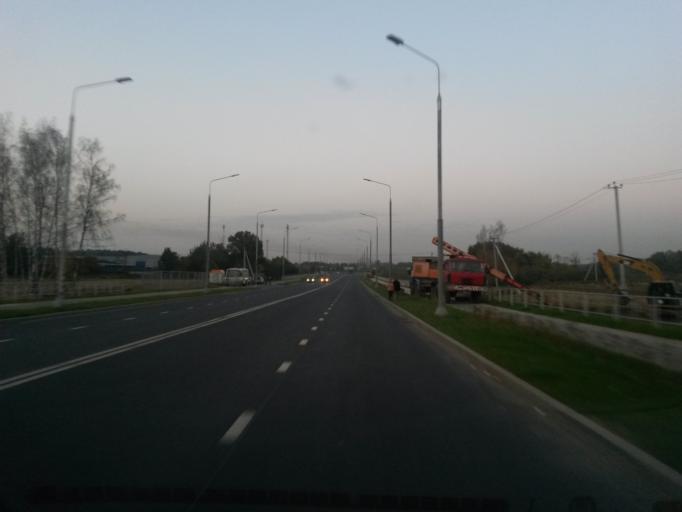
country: RU
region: Moskovskaya
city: Kommunarka
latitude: 55.5512
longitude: 37.4871
